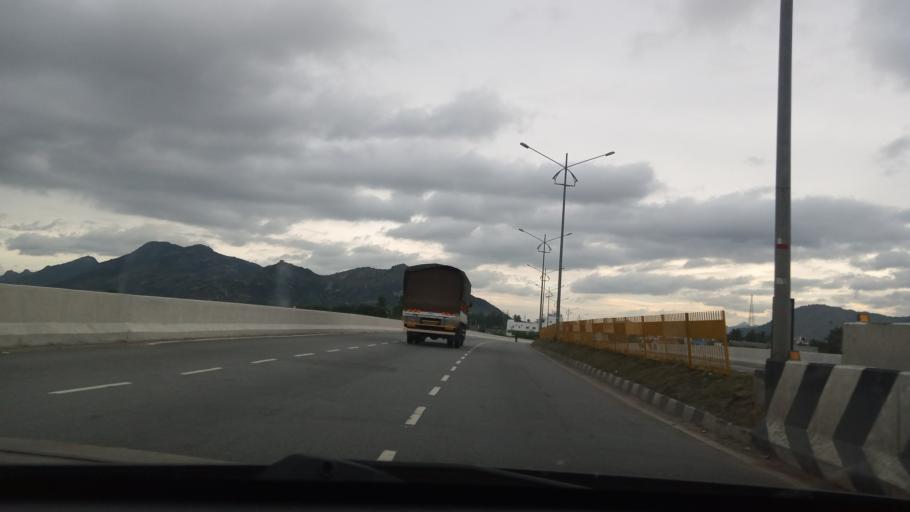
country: IN
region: Tamil Nadu
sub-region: Krishnagiri
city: Krishnagiri
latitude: 12.5154
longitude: 78.2307
